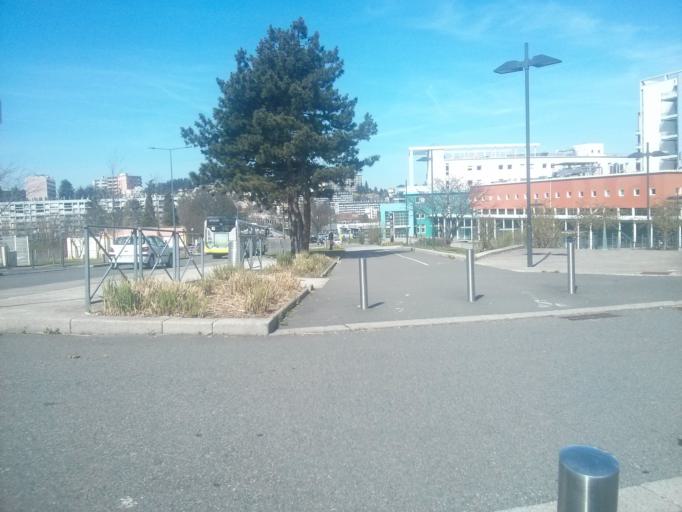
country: FR
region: Rhone-Alpes
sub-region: Departement de la Loire
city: Saint-Etienne
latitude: 45.4270
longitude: 4.4188
